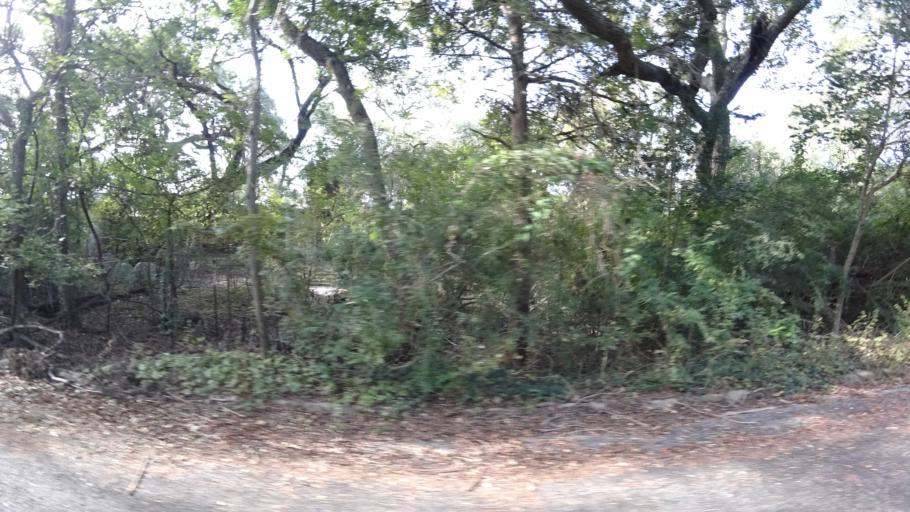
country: US
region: Texas
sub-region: Travis County
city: Austin
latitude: 30.2052
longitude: -97.7346
